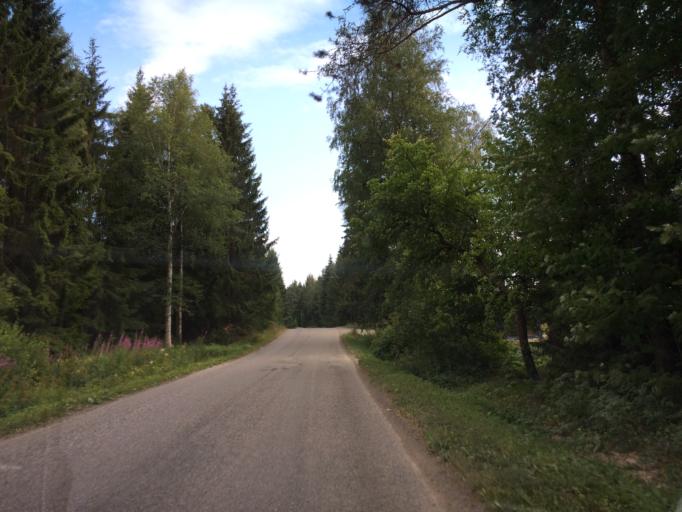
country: FI
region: Haeme
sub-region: Haemeenlinna
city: Hauho
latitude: 61.0771
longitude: 24.6630
